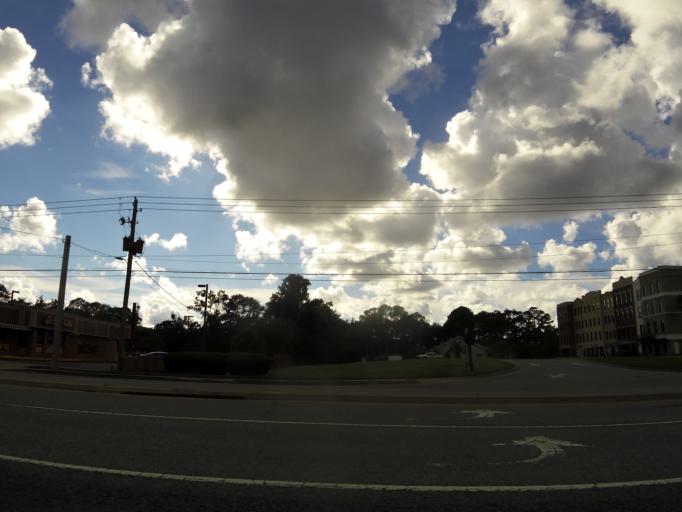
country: US
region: Georgia
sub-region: Glynn County
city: Brunswick
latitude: 31.1715
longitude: -81.4743
